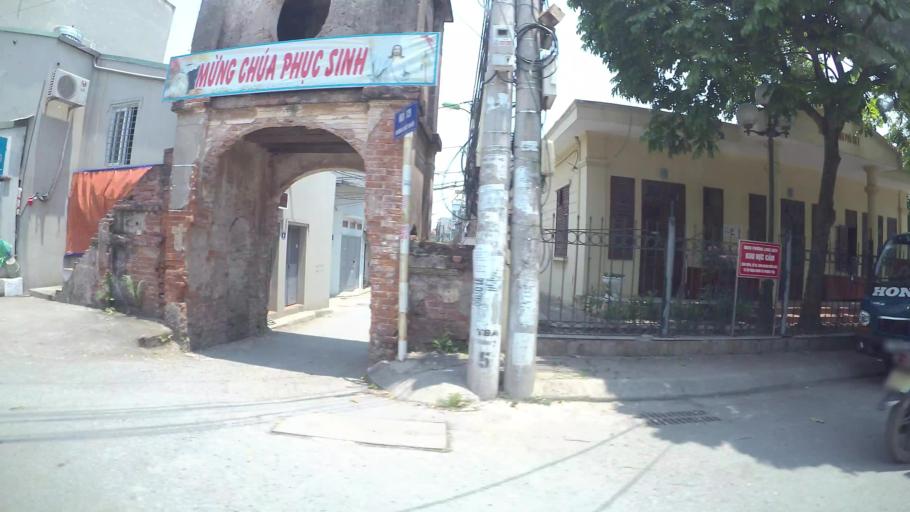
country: VN
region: Ha Noi
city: Hoan Kiem
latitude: 21.0245
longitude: 105.8853
